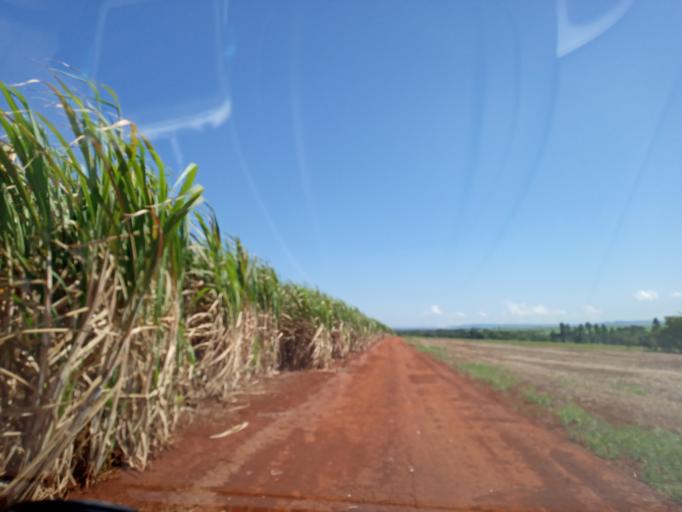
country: BR
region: Goias
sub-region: Itumbiara
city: Itumbiara
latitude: -18.4434
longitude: -49.1451
